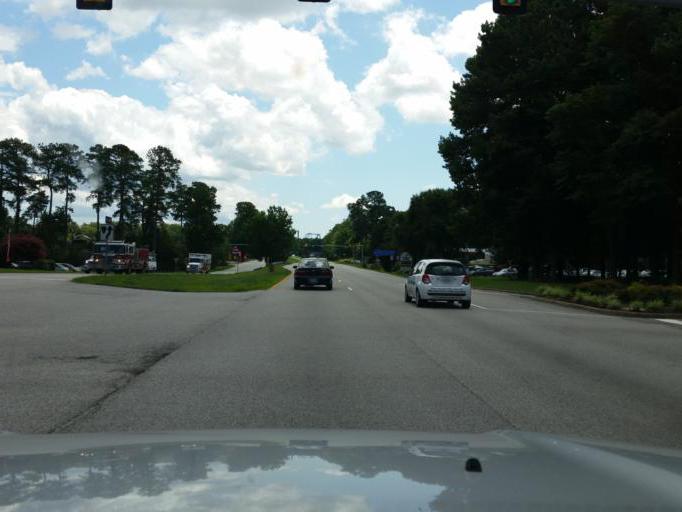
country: US
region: Virginia
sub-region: City of Williamsburg
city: Williamsburg
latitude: 37.2481
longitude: -76.6596
